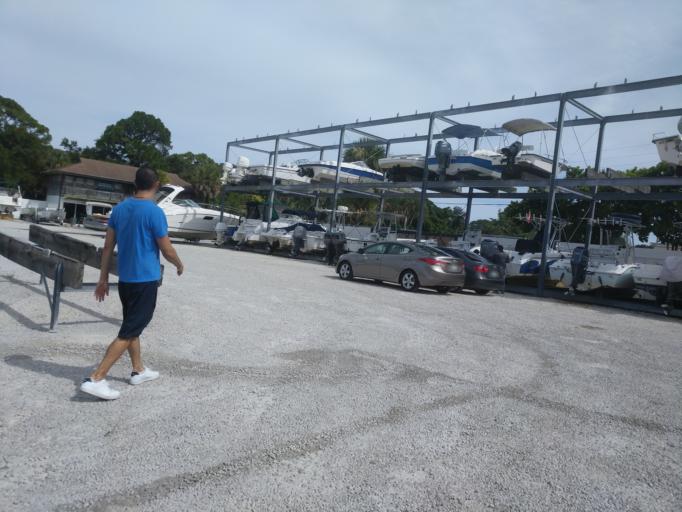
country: US
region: Florida
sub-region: Broward County
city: Deerfield Beach
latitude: 26.3275
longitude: -80.1036
